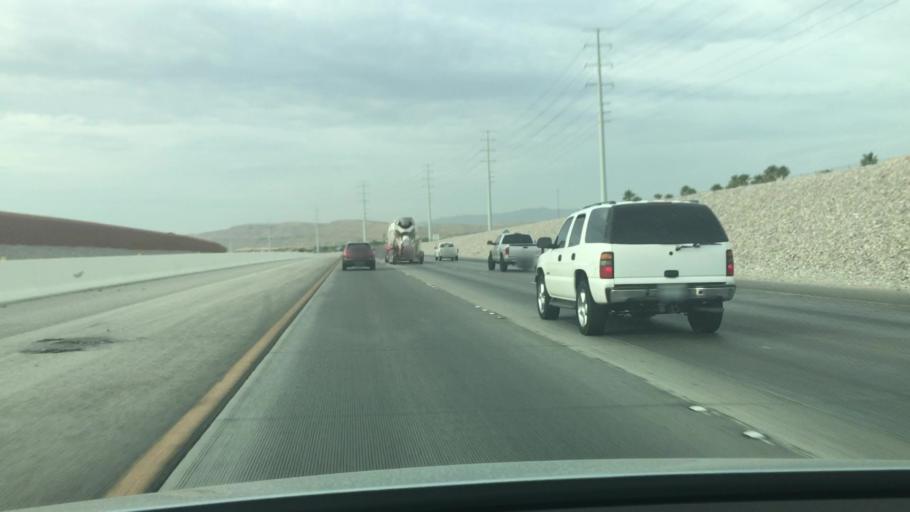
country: US
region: Nevada
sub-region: Clark County
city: Summerlin South
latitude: 36.1377
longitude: -115.3365
